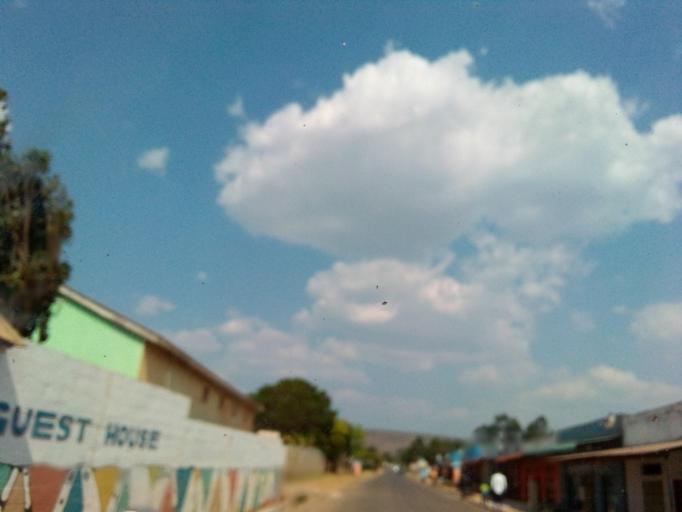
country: ZM
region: Northern
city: Mpika
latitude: -11.8441
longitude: 31.4443
